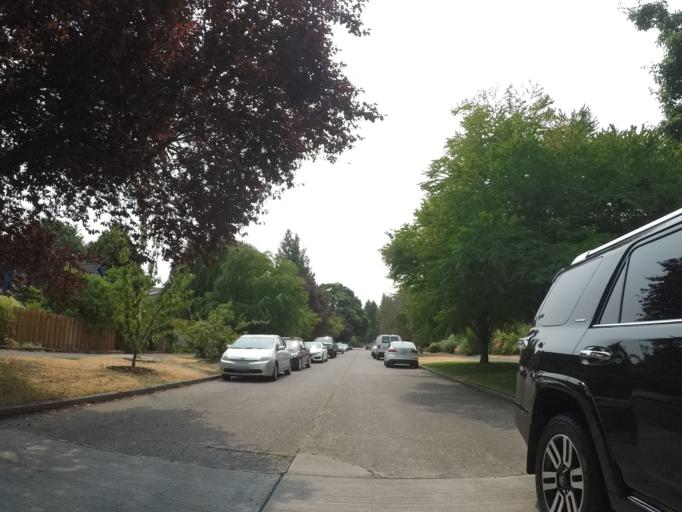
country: US
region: Washington
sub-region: King County
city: Seattle
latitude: 47.5826
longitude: -122.3892
